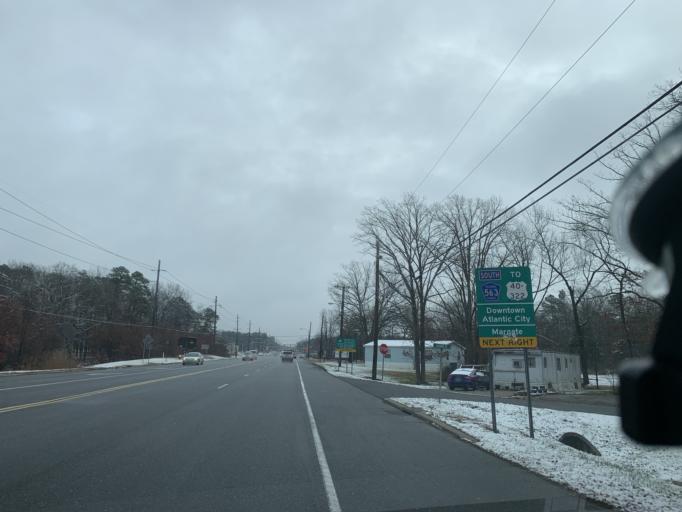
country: US
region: New Jersey
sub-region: Atlantic County
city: Pomona
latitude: 39.4325
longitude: -74.5822
